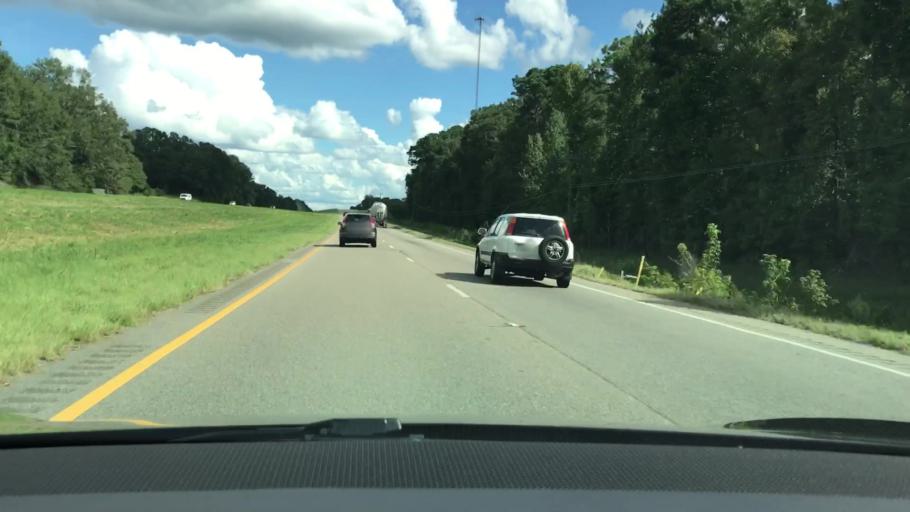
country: US
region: Alabama
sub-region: Montgomery County
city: Pike Road
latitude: 32.1318
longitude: -86.0854
